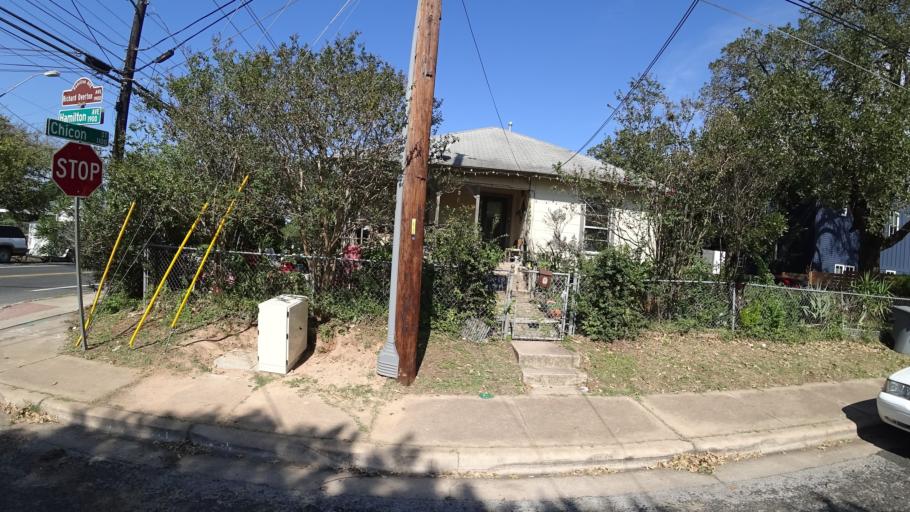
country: US
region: Texas
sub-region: Travis County
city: Austin
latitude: 30.2676
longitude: -97.7196
